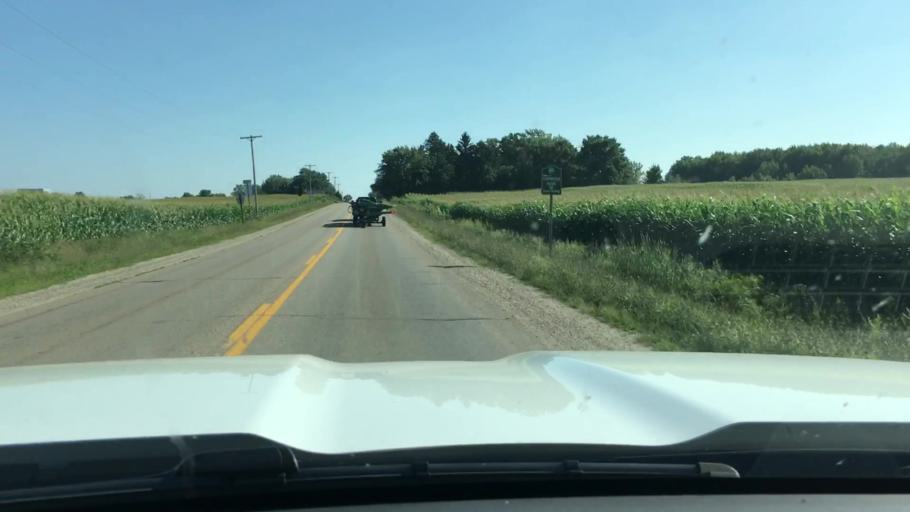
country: US
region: Michigan
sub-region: Ottawa County
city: Coopersville
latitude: 43.0738
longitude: -85.9569
